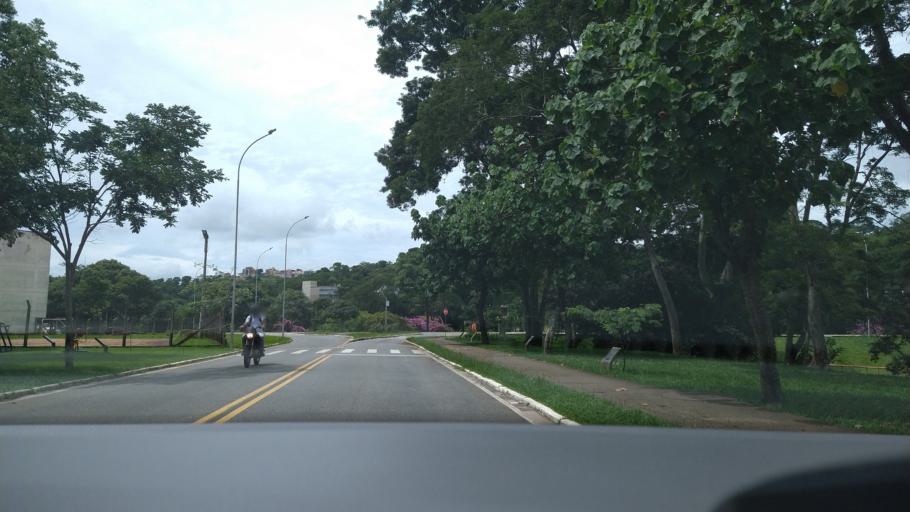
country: BR
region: Minas Gerais
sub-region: Vicosa
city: Vicosa
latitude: -20.7612
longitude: -42.8717
